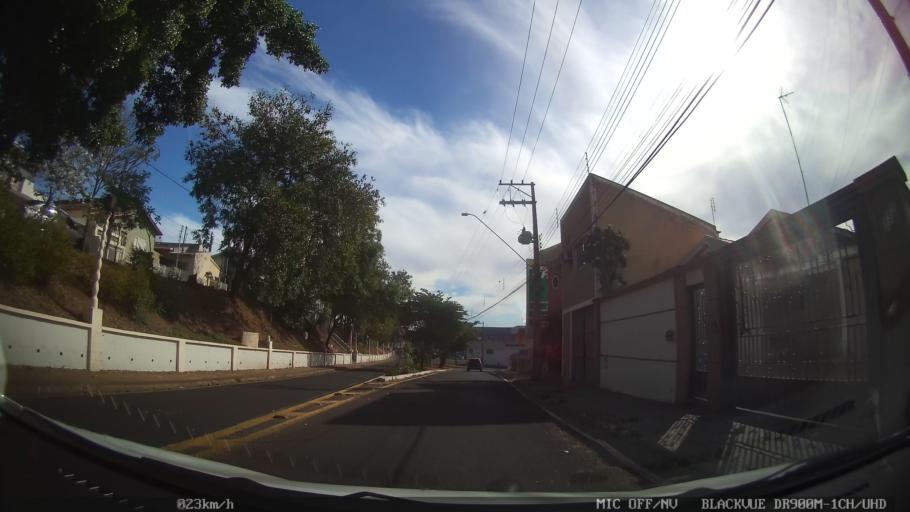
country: BR
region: Sao Paulo
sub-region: Catanduva
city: Catanduva
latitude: -21.1294
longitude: -48.9808
